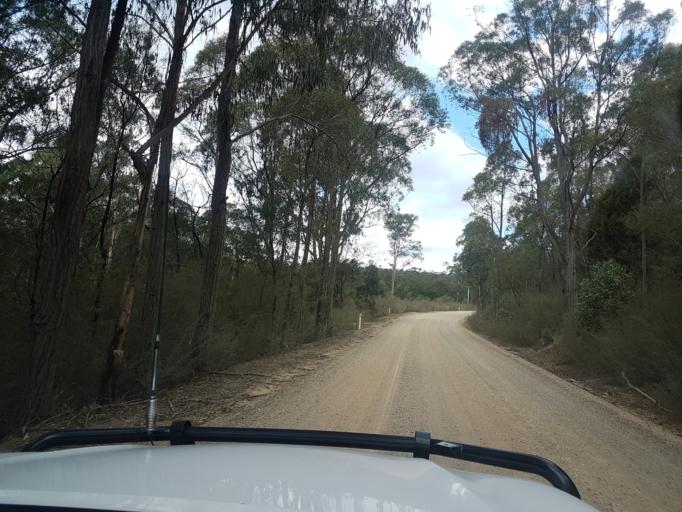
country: AU
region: Victoria
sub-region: East Gippsland
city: Bairnsdale
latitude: -37.6805
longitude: 147.5527
